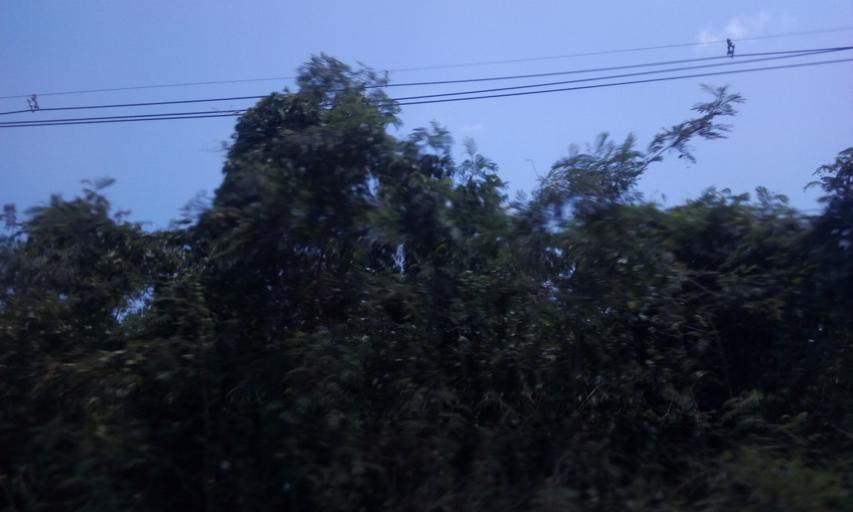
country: TH
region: Chachoengsao
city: Bang Nam Priao
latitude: 13.8410
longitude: 101.0529
